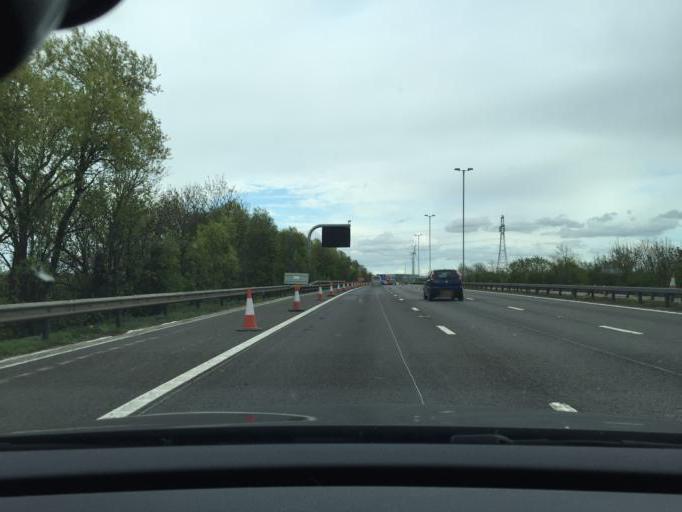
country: GB
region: England
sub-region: West Berkshire
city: Calcot
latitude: 51.4207
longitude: -1.0064
